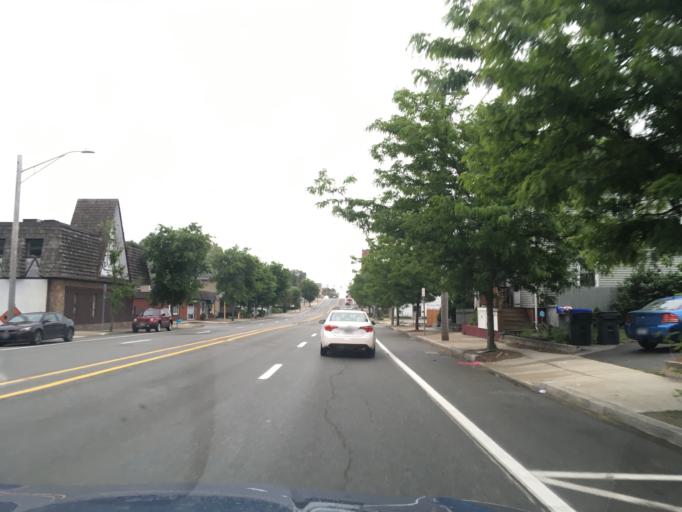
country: US
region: Rhode Island
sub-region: Providence County
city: Cranston
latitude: 41.7788
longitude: -71.4208
